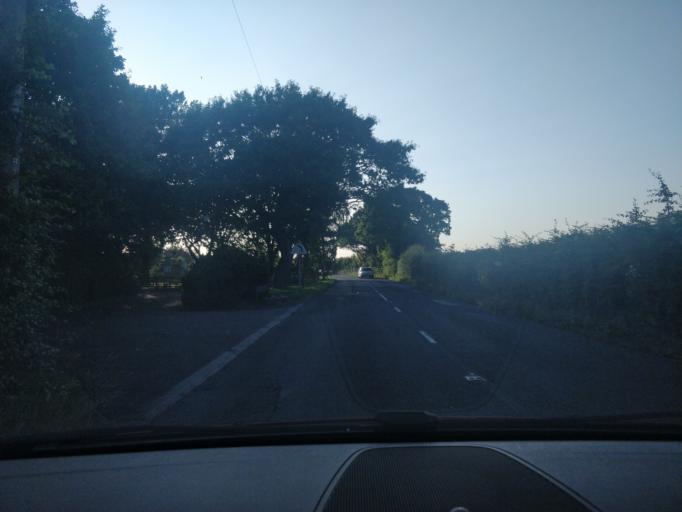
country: GB
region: England
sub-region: Lancashire
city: Parbold
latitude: 53.6057
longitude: -2.7719
